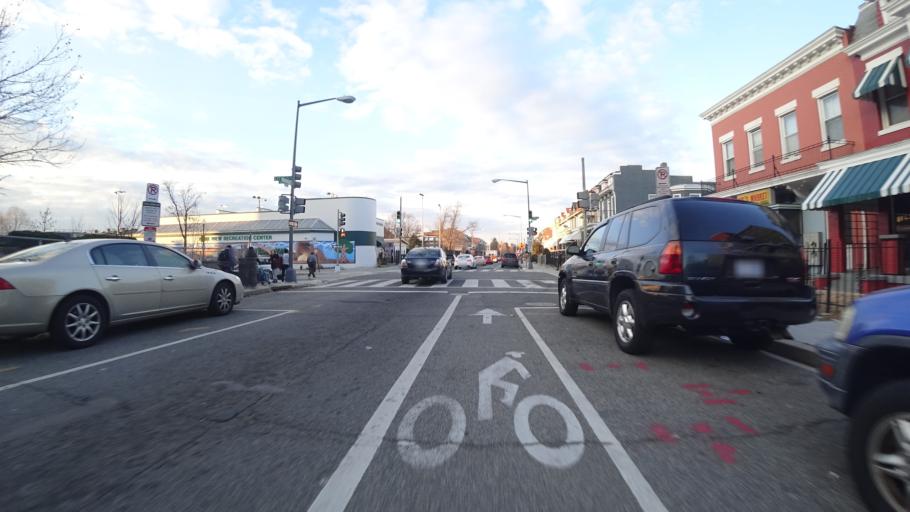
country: US
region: Maryland
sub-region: Prince George's County
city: Chillum
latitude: 38.9347
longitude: -77.0210
